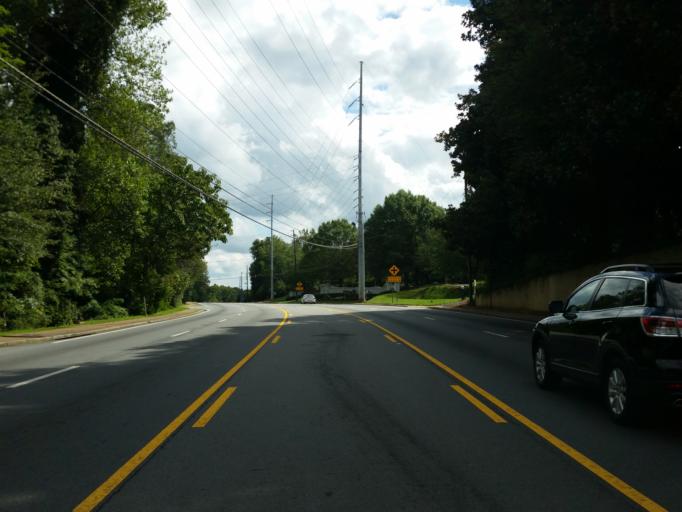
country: US
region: Georgia
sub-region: Cobb County
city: Marietta
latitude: 33.9438
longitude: -84.5515
